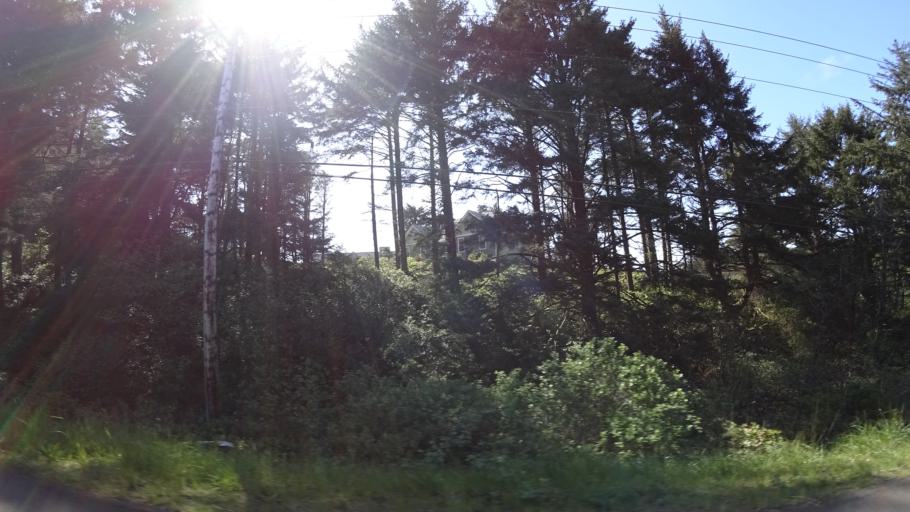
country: US
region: Oregon
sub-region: Lincoln County
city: Newport
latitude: 44.5722
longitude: -124.0673
